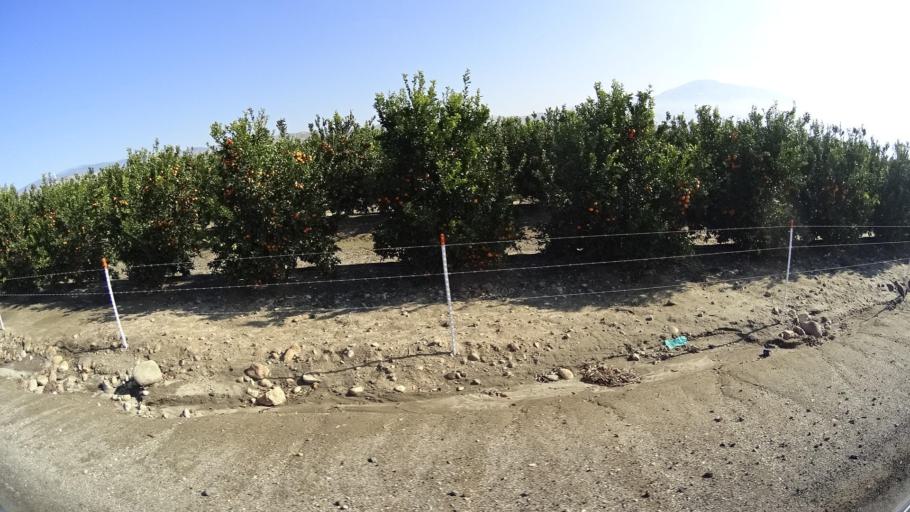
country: US
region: California
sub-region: Kern County
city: Arvin
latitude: 35.2781
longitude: -118.7707
